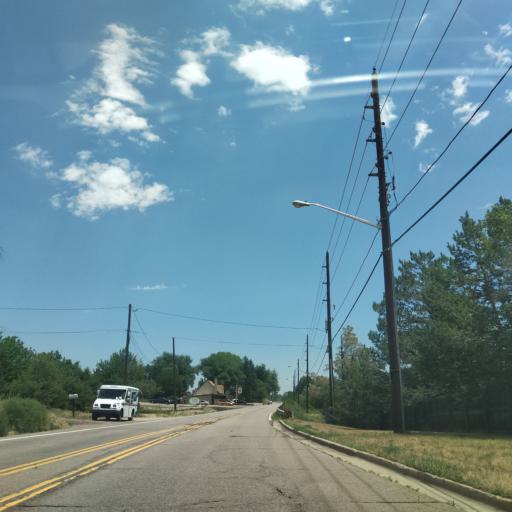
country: US
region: Colorado
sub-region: Jefferson County
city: Lakewood
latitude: 39.6749
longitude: -105.0869
